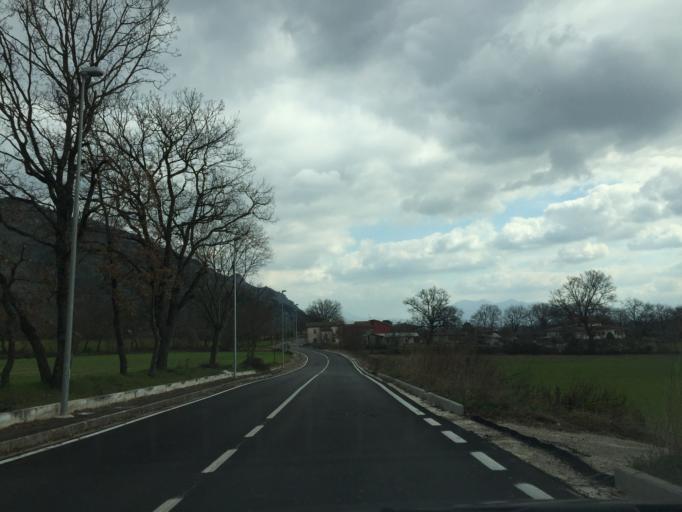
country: IT
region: Latium
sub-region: Provincia di Frosinone
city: Villa Santa Lucia
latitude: 41.4960
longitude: 13.7692
